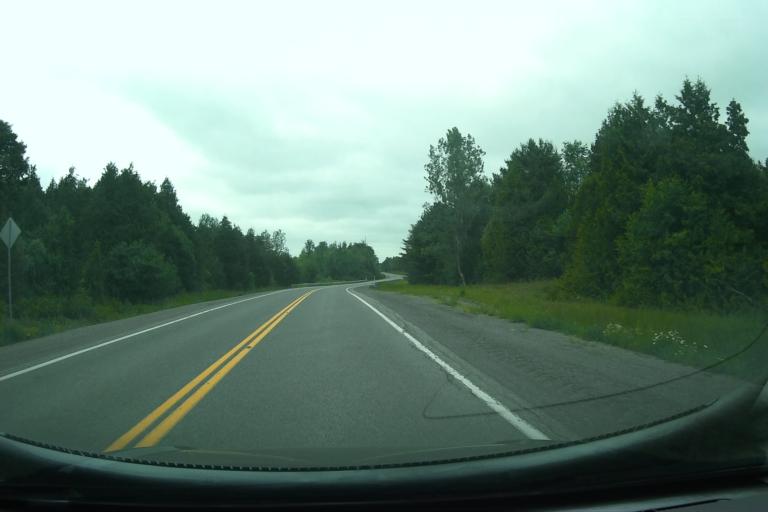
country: CA
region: Ontario
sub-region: Lanark County
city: Smiths Falls
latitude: 45.0179
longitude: -75.8455
